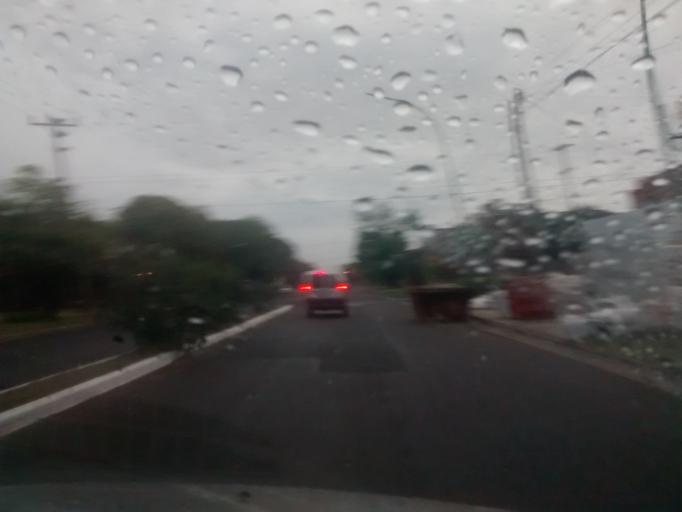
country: AR
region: Buenos Aires
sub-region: Partido de La Plata
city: La Plata
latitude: -34.9064
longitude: -58.0158
